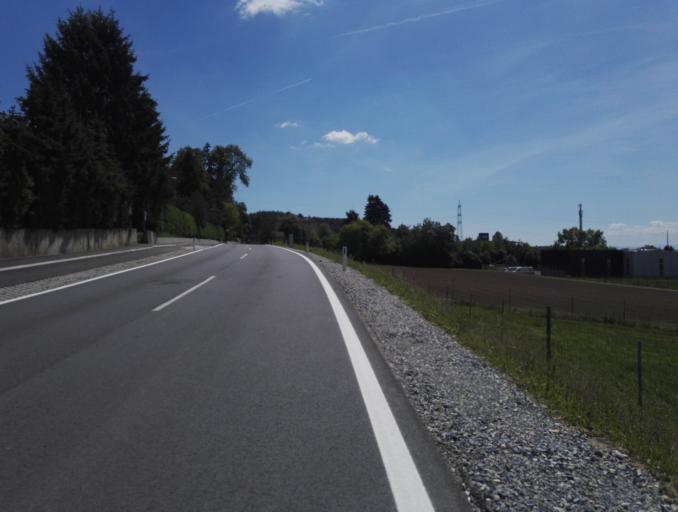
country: AT
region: Styria
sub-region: Politischer Bezirk Graz-Umgebung
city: Grambach
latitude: 47.0225
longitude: 15.4995
